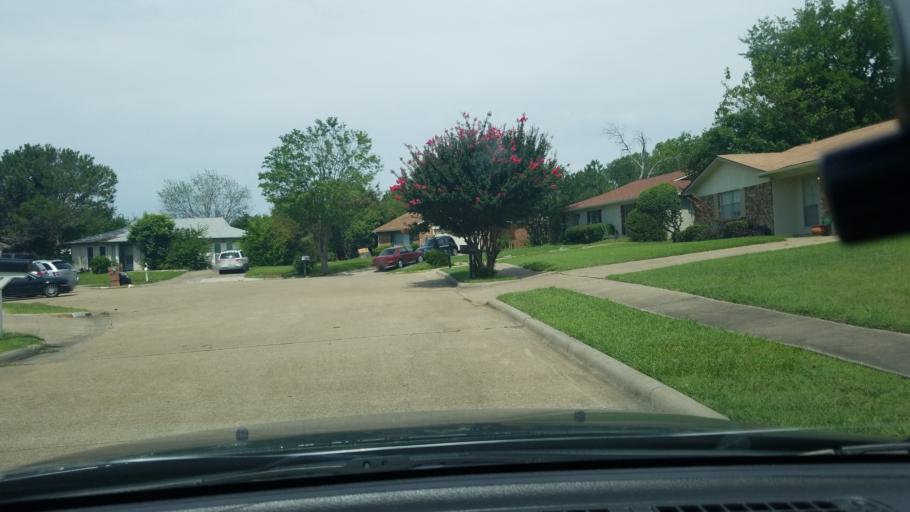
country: US
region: Texas
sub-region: Dallas County
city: Mesquite
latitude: 32.7588
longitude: -96.5778
